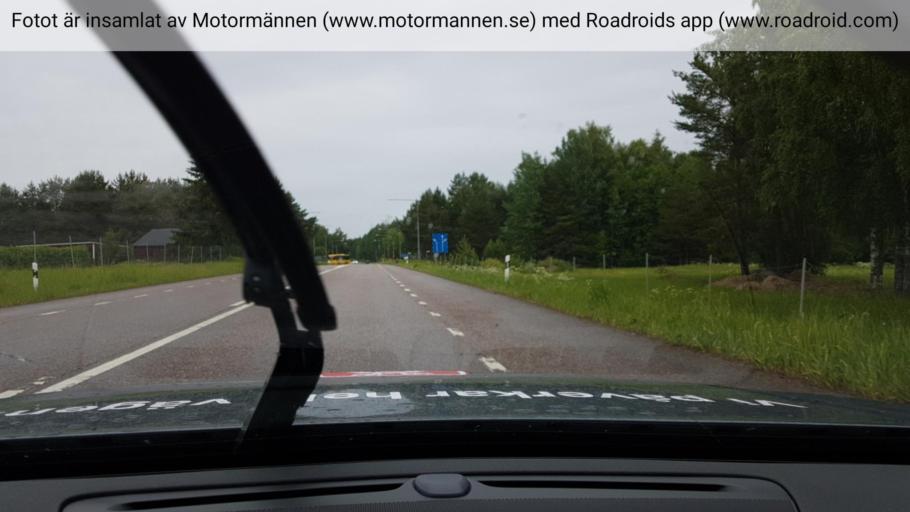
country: SE
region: Uppsala
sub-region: Alvkarleby Kommun
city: AElvkarleby
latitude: 60.5826
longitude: 17.4655
